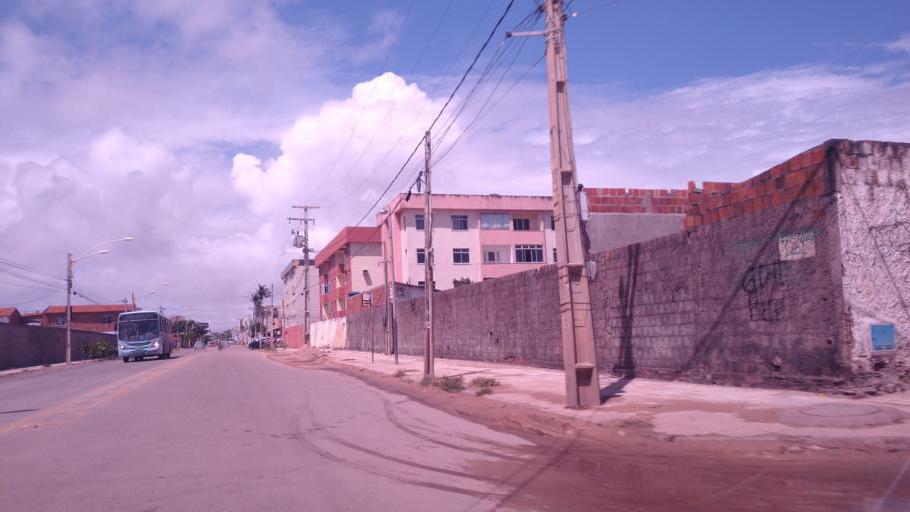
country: BR
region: Ceara
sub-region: Fortaleza
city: Fortaleza
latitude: -3.7207
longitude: -38.4646
